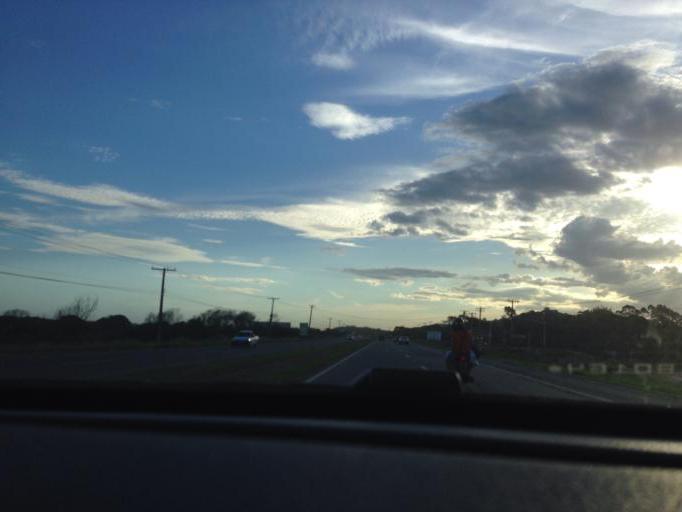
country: BR
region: Espirito Santo
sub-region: Vila Velha
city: Vila Velha
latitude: -20.4557
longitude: -40.3394
